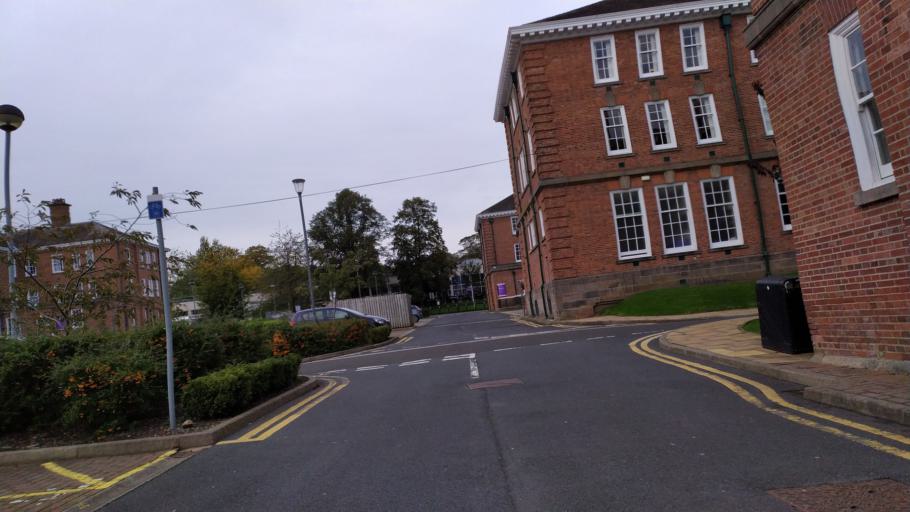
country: GB
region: England
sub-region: City and Borough of Leeds
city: Horsforth
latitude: 53.8264
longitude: -1.5909
